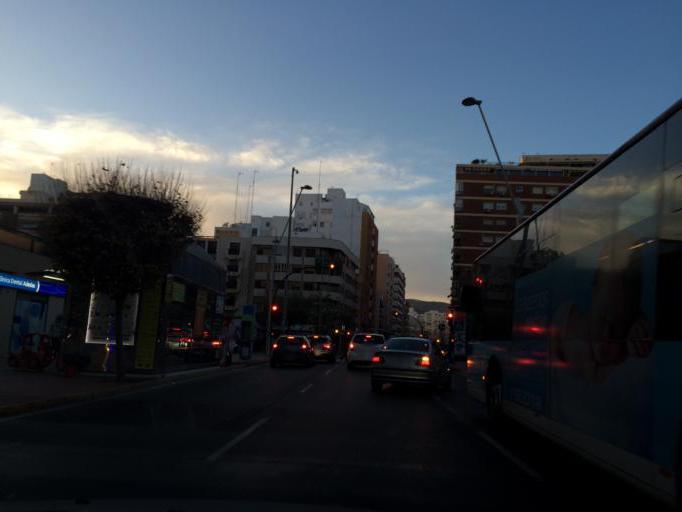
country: ES
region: Andalusia
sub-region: Provincia de Almeria
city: Almeria
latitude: 36.8389
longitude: -2.4590
